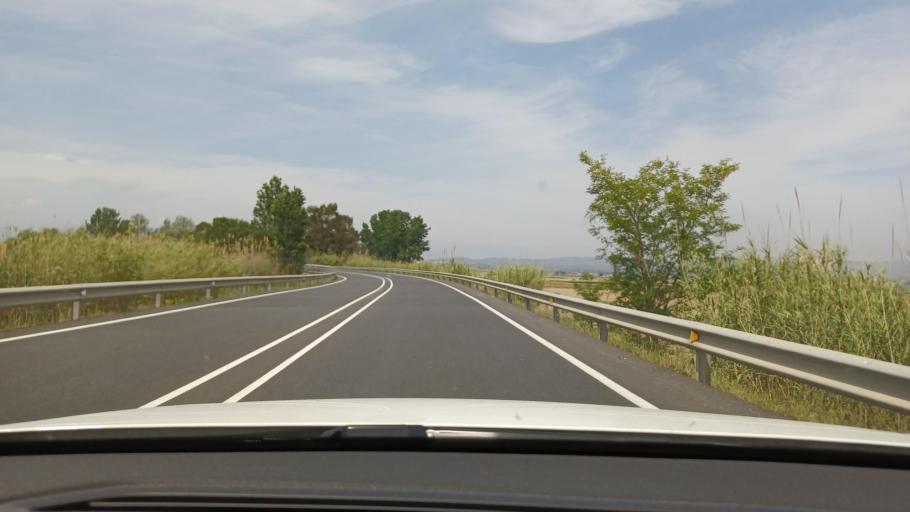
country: ES
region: Catalonia
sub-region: Provincia de Tarragona
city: Deltebre
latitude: 40.7294
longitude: 0.6850
